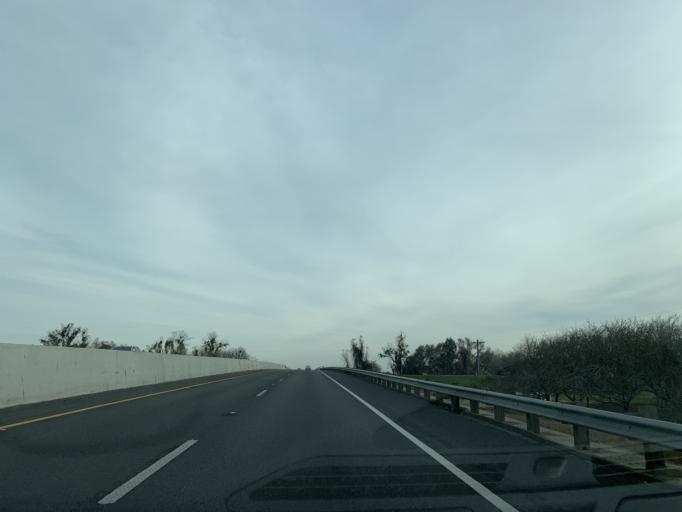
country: US
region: California
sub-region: Yuba County
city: Plumas Lake
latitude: 38.9076
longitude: -121.5934
